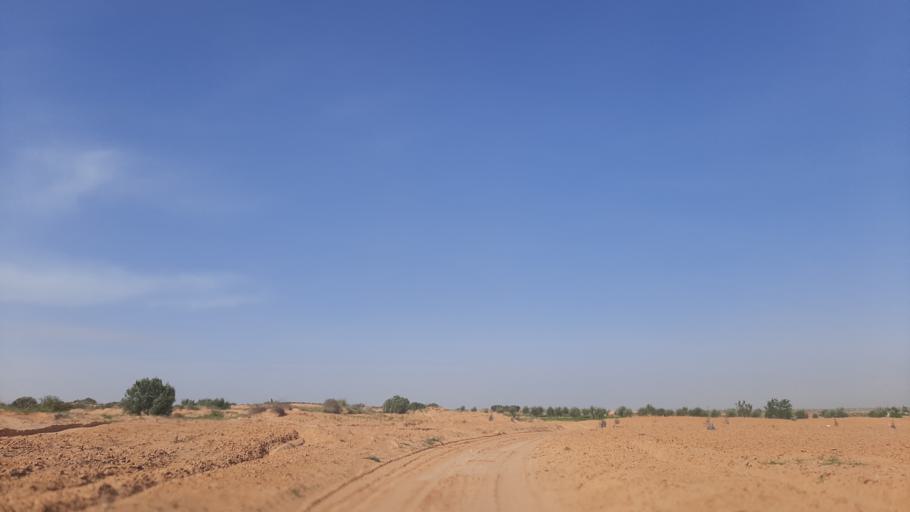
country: TN
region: Madanin
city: Zarzis
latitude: 33.4342
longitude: 10.8089
